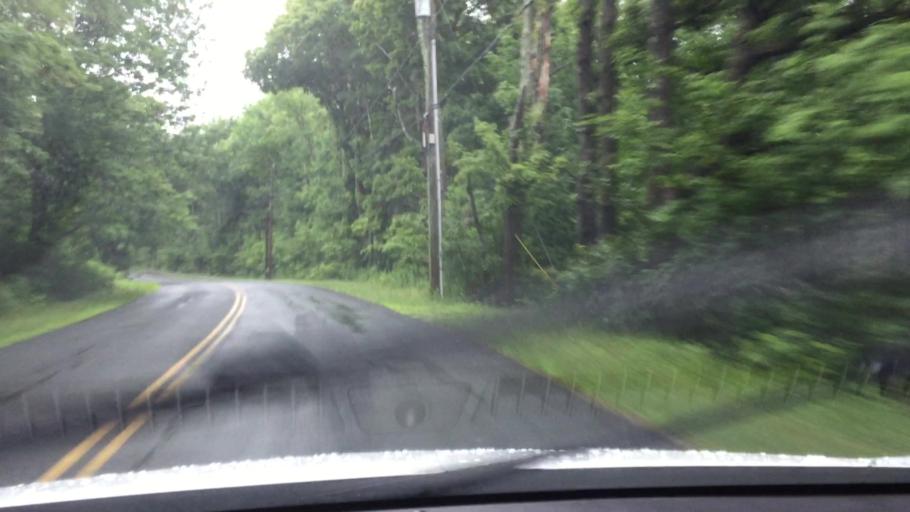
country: US
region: Massachusetts
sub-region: Berkshire County
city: Becket
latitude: 42.3194
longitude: -73.0959
